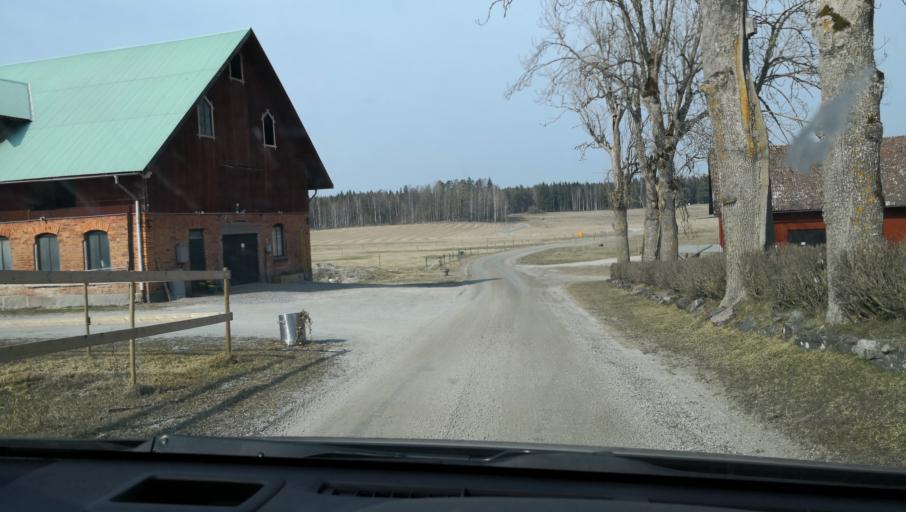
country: SE
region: OErebro
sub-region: Lindesbergs Kommun
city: Frovi
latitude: 59.3515
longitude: 15.4366
